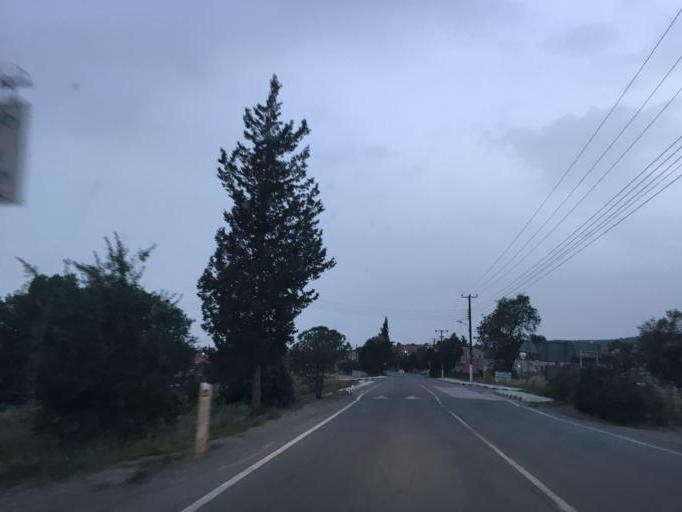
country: CY
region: Limassol
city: Parekklisha
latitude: 34.7468
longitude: 33.1579
